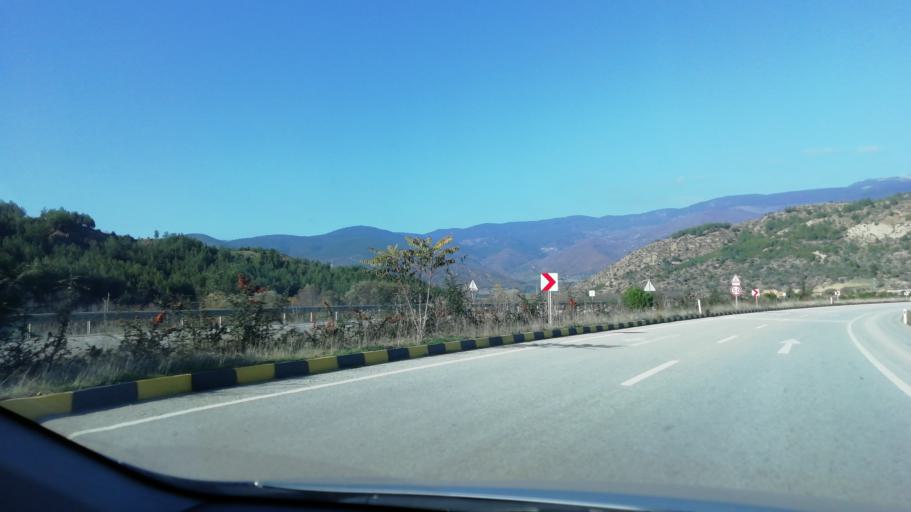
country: TR
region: Karabuk
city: Eskipazar
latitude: 40.9823
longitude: 32.5618
